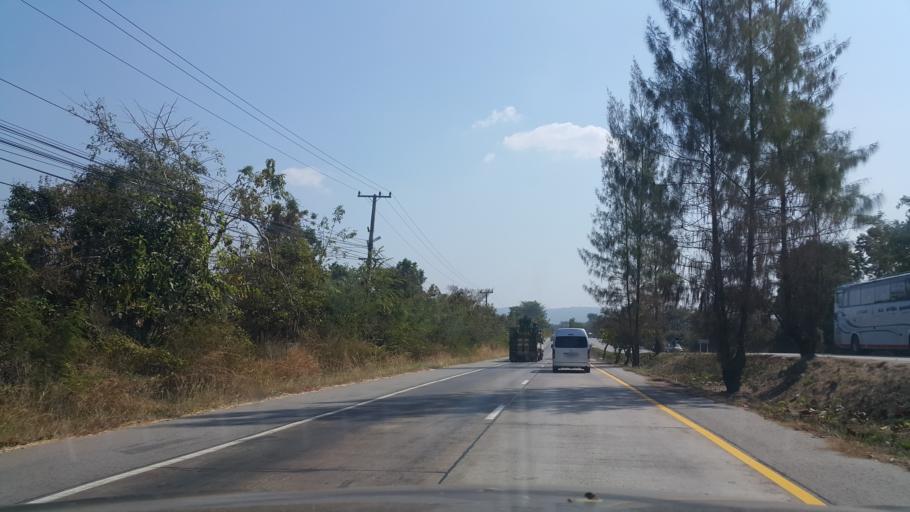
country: TH
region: Changwat Udon Thani
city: Non Sa-at
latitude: 16.8964
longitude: 102.8739
